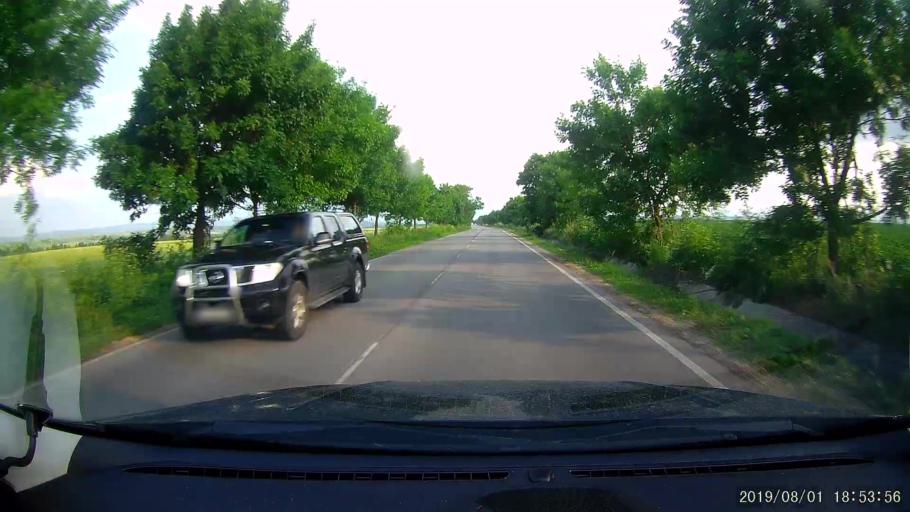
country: BG
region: Shumen
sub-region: Obshtina Shumen
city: Shumen
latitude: 43.2113
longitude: 26.9985
